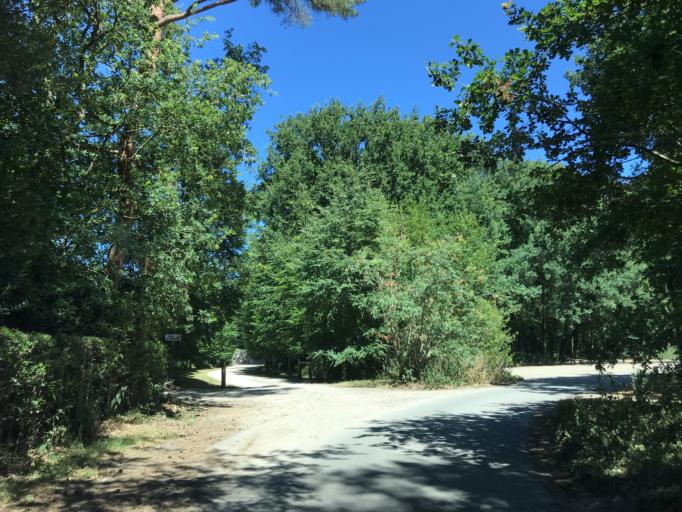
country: NL
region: North Holland
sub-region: Gemeente Huizen
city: Huizen
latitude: 52.3050
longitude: 5.2145
